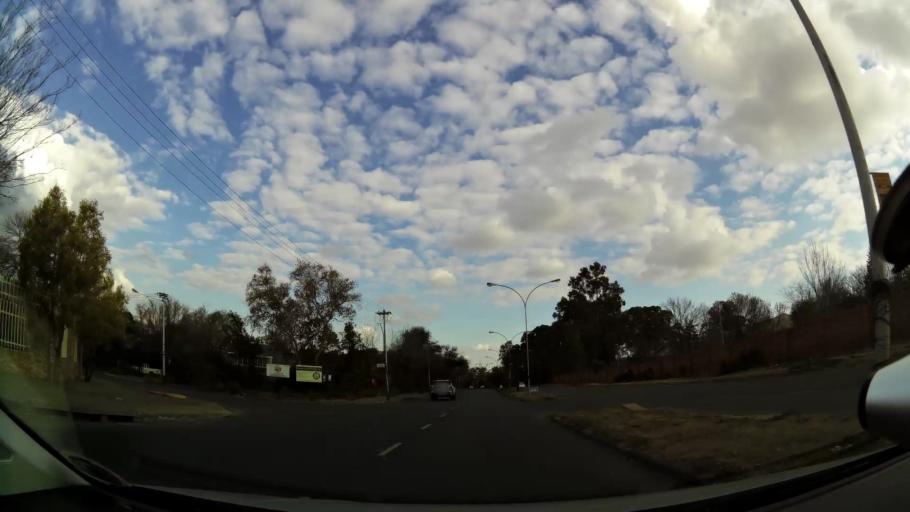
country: ZA
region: Orange Free State
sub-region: Mangaung Metropolitan Municipality
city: Bloemfontein
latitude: -29.0916
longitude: 26.2037
